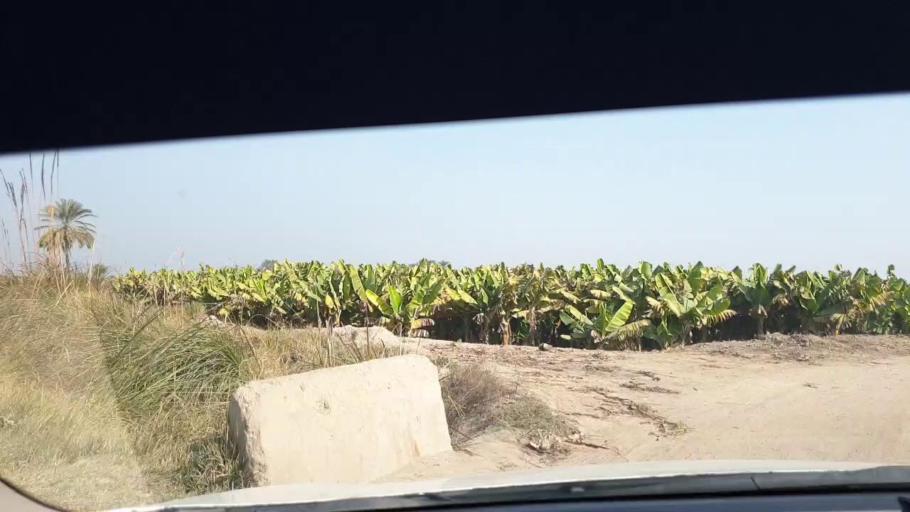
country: PK
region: Sindh
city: Tando Adam
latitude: 25.7402
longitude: 68.7026
